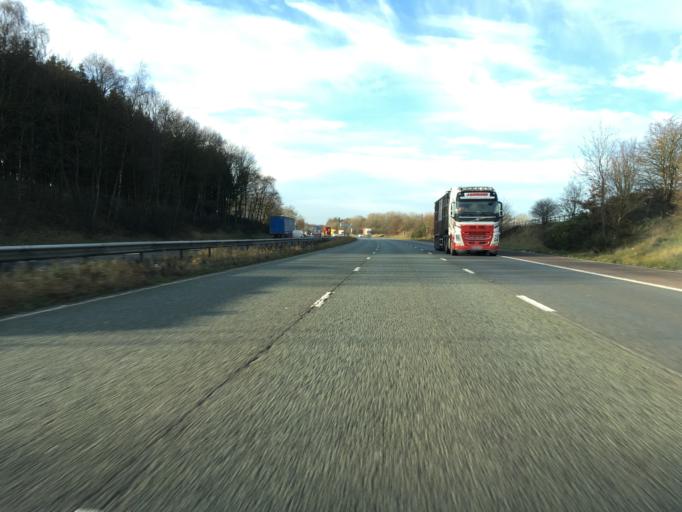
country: GB
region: England
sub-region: Warrington
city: Lymm
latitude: 53.3631
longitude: -2.4524
